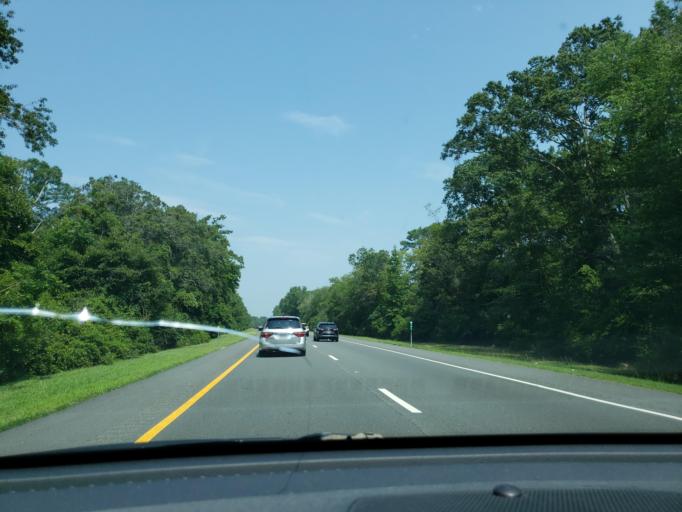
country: US
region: New Jersey
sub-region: Cape May County
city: Avalon
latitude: 39.1370
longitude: -74.7639
